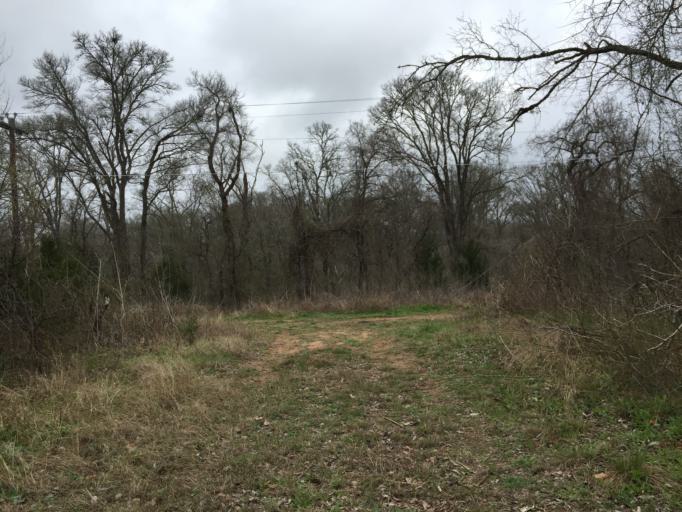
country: US
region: Texas
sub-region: Bastrop County
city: Bastrop
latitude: 30.0820
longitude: -97.3227
